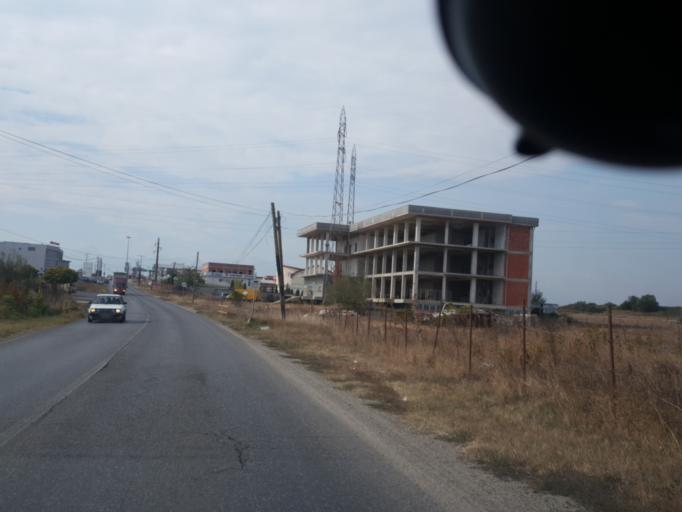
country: XK
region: Gjakova
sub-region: Komuna e Gjakoves
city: Gjakove
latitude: 42.3670
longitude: 20.4647
